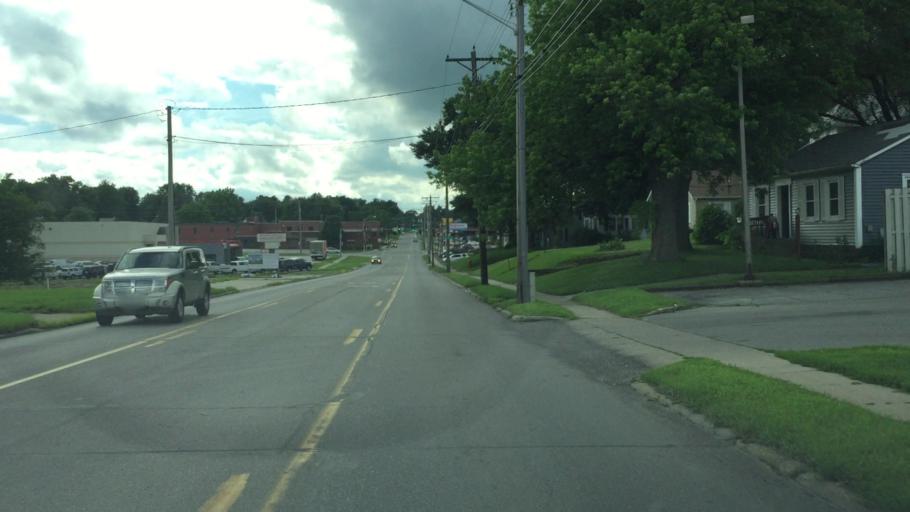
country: US
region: Iowa
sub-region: Jasper County
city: Newton
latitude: 41.6992
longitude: -93.0359
